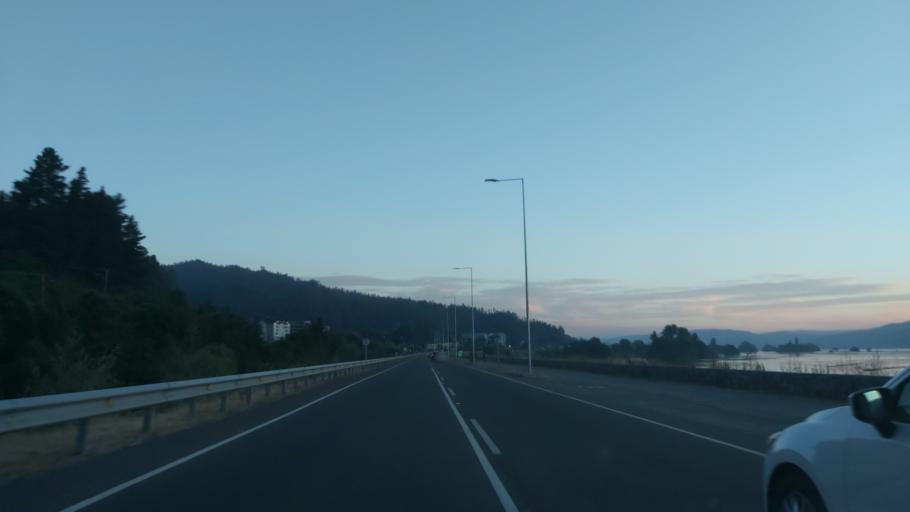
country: CL
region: Biobio
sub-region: Provincia de Concepcion
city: Concepcion
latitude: -36.8741
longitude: -73.0418
